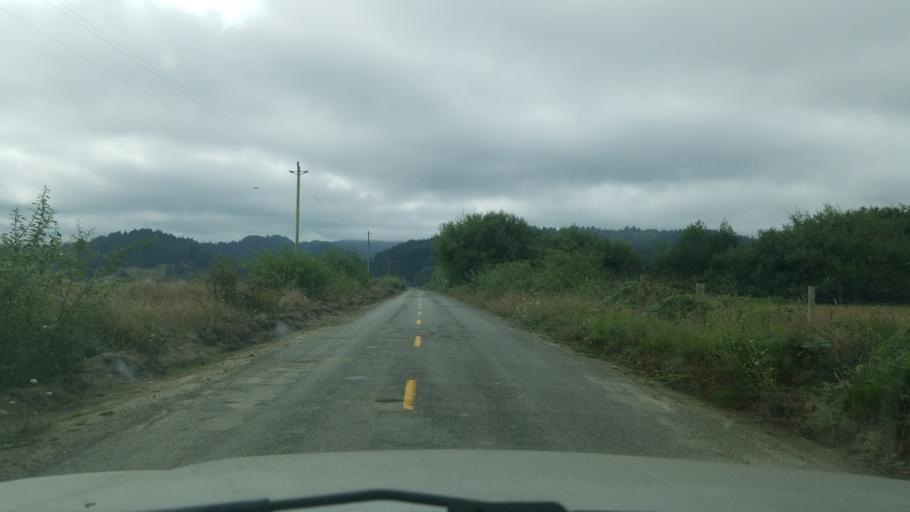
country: US
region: California
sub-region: Humboldt County
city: Ferndale
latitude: 40.5940
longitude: -124.2841
